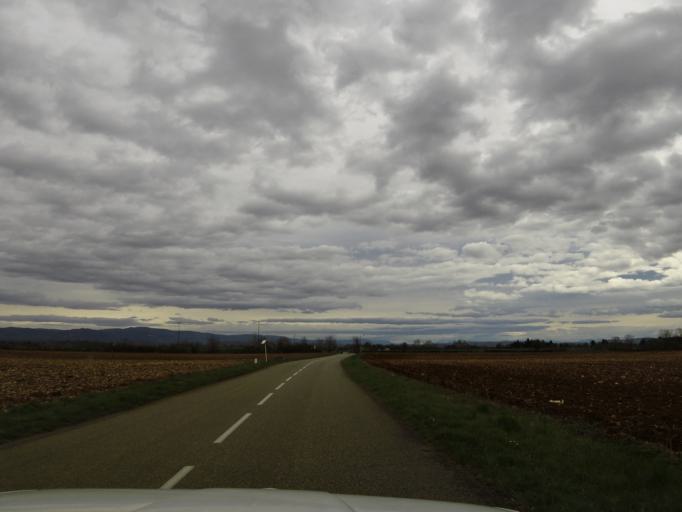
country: FR
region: Rhone-Alpes
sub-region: Departement de l'Ain
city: Meximieux
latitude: 45.8961
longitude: 5.2086
